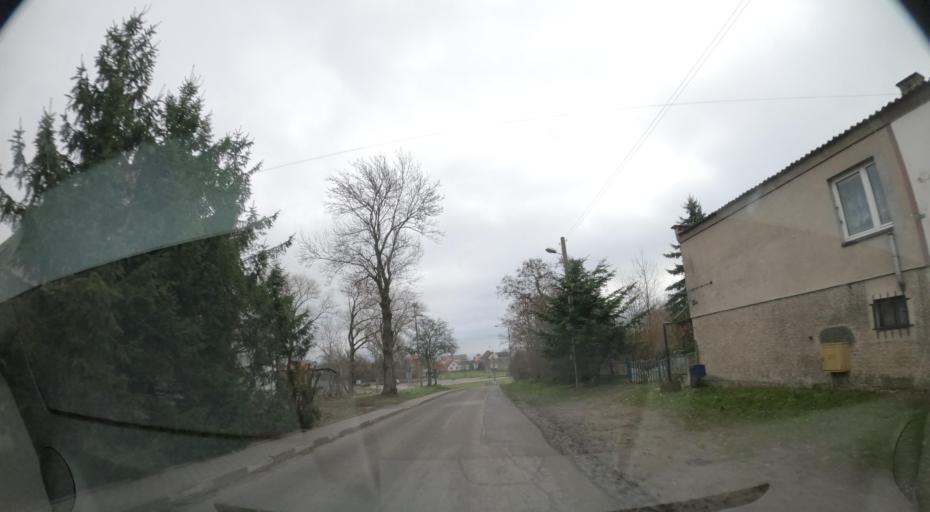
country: PL
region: Greater Poland Voivodeship
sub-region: Powiat pilski
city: Lobzenica
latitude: 53.2593
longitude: 17.2490
